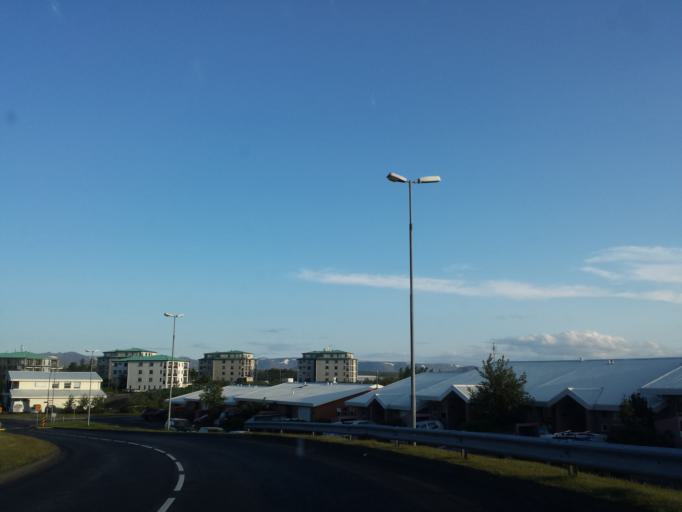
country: IS
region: Capital Region
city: Mosfellsbaer
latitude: 64.1073
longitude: -21.7889
